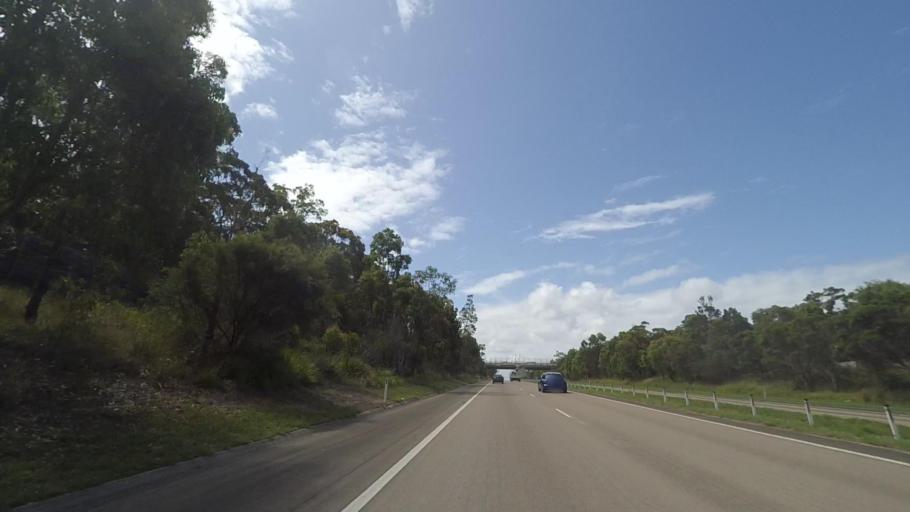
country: AU
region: New South Wales
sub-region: Lake Macquarie Shire
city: Gateshead
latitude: -32.9768
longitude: 151.6786
